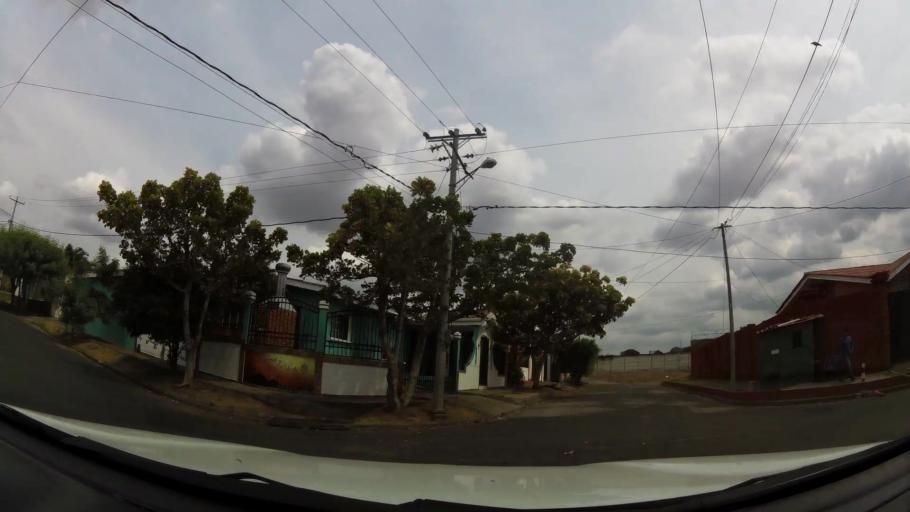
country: NI
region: Managua
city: Managua
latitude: 12.1068
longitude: -86.2449
